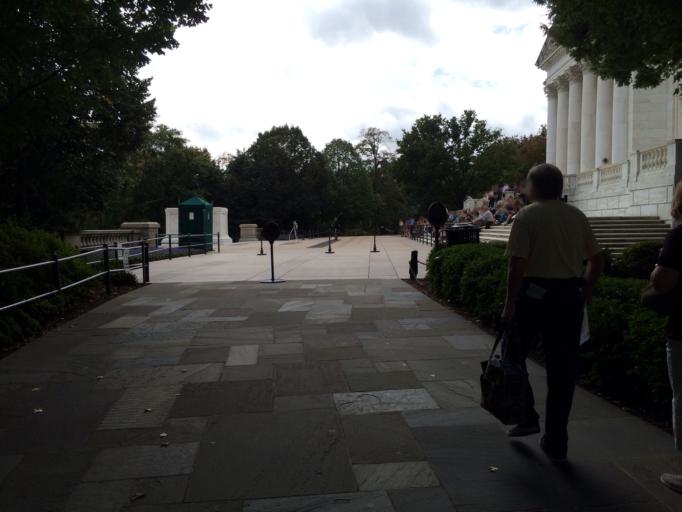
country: US
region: Virginia
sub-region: Arlington County
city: Arlington
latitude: 38.8768
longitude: -77.0723
